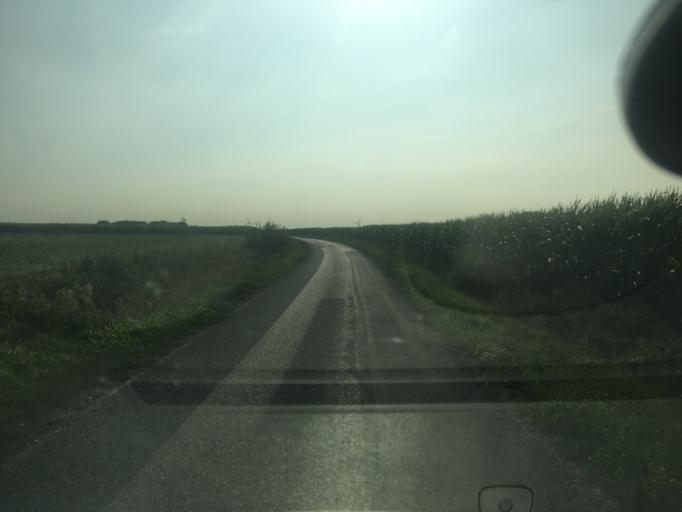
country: DK
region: South Denmark
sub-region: Tonder Kommune
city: Logumkloster
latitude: 54.9955
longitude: 8.9156
